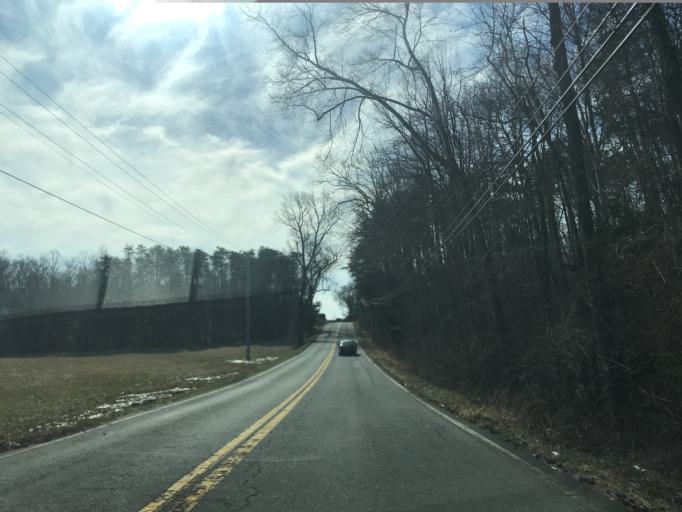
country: US
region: Maryland
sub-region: Charles County
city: Potomac Heights
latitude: 38.5699
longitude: -77.1269
